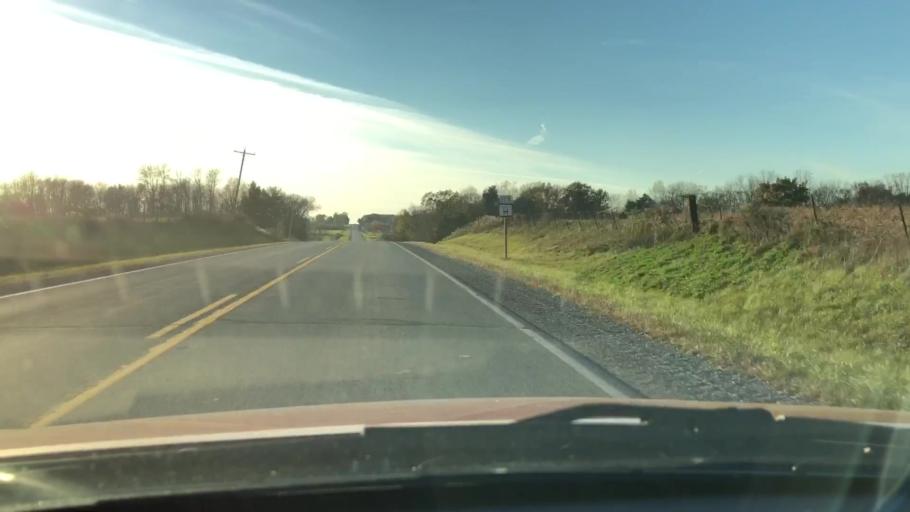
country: US
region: Wisconsin
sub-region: Brown County
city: Oneida
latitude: 44.4444
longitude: -88.2468
